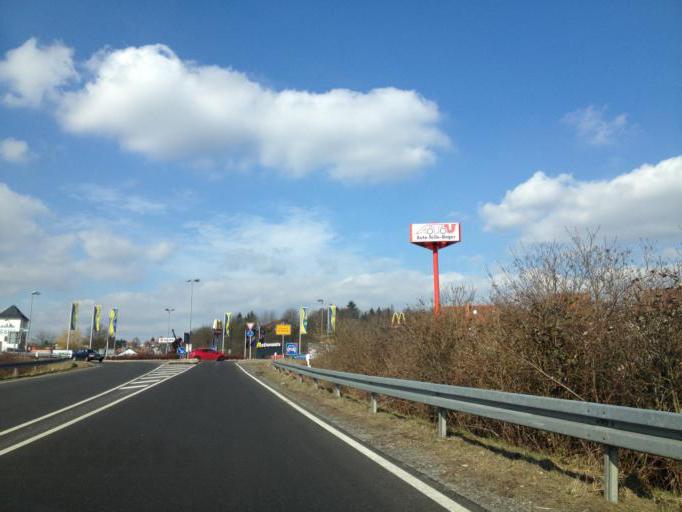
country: DE
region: Saarland
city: Sankt Wendel
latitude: 49.4610
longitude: 7.1582
